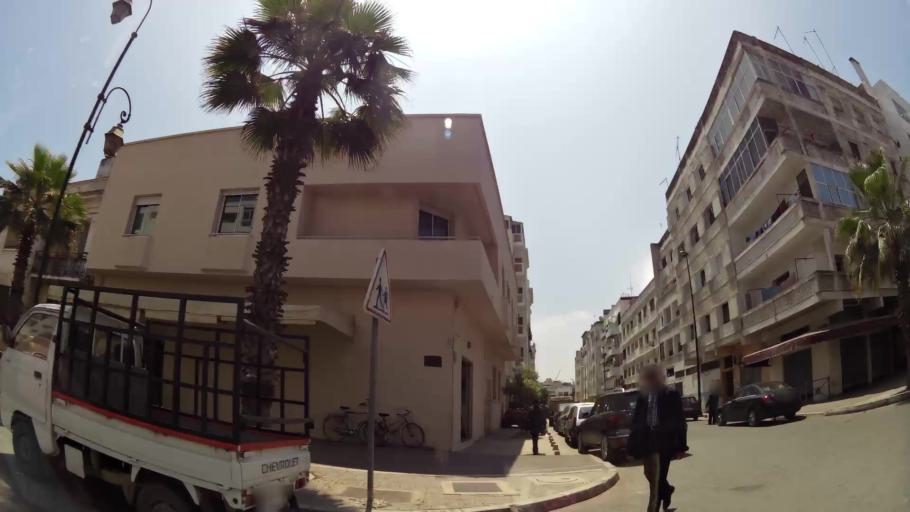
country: MA
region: Rabat-Sale-Zemmour-Zaer
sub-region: Rabat
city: Rabat
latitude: 34.0241
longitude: -6.8449
